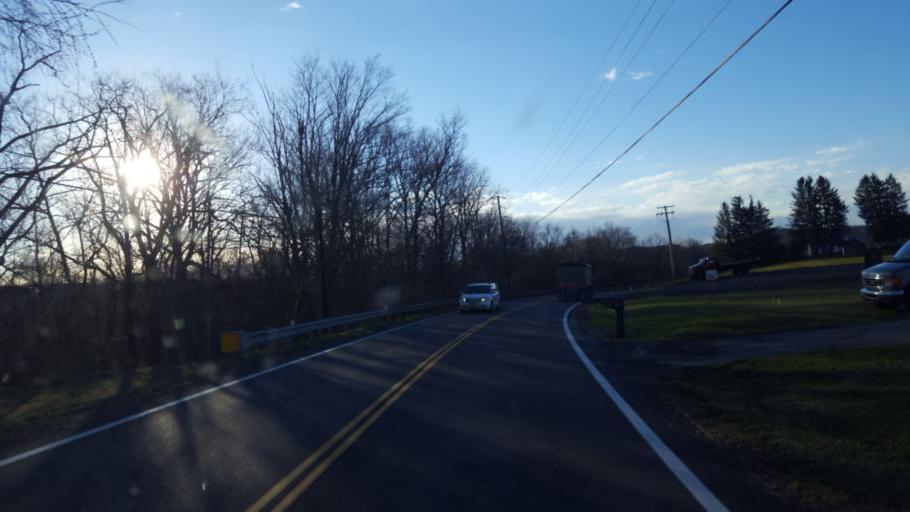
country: US
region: Ohio
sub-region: Ashland County
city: Loudonville
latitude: 40.6458
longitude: -82.2452
